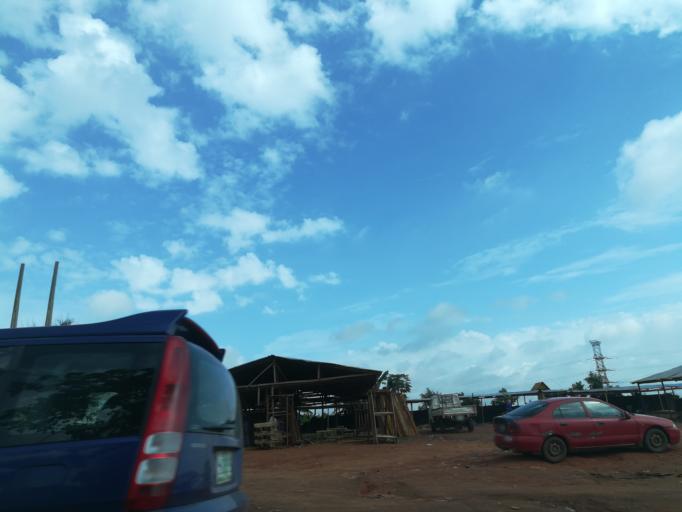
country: NG
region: Lagos
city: Ikorodu
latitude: 6.6348
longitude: 3.5377
